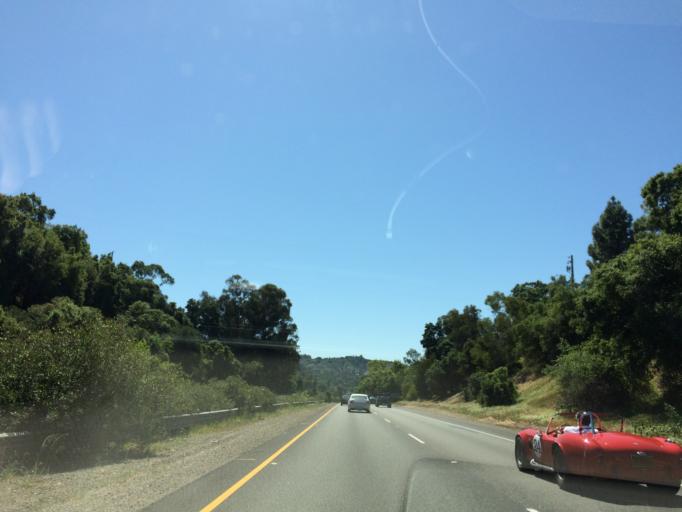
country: US
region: California
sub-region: Santa Clara County
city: Los Gatos
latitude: 37.2329
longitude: -121.9717
